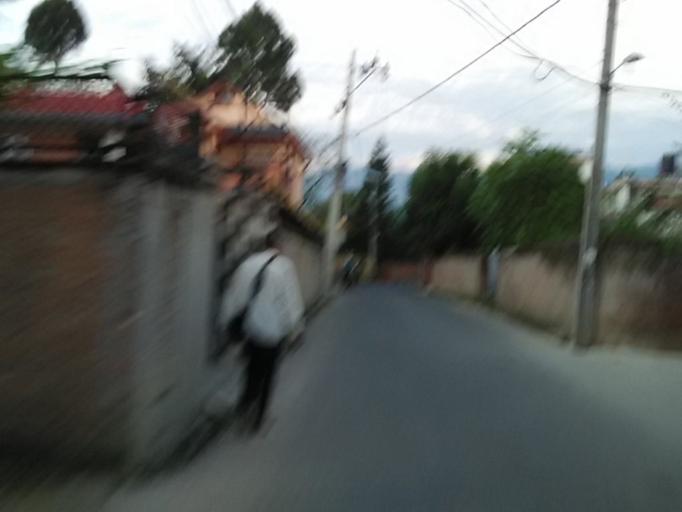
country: NP
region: Central Region
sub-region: Bagmati Zone
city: Kathmandu
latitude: 27.7336
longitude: 85.3364
